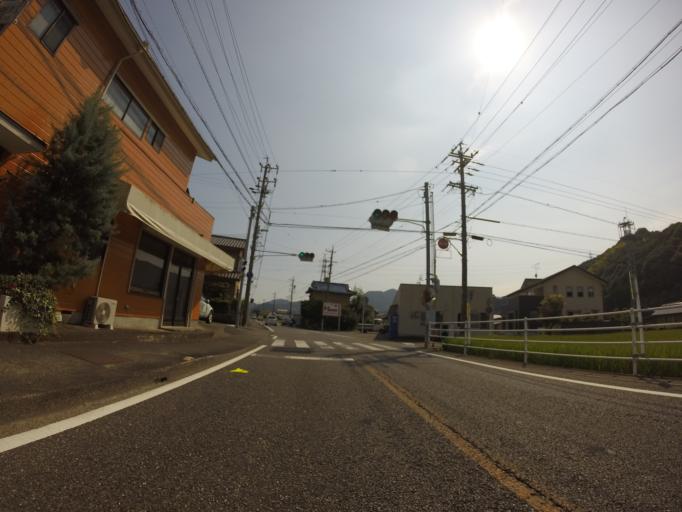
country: JP
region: Shizuoka
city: Shizuoka-shi
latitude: 35.0270
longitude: 138.3628
